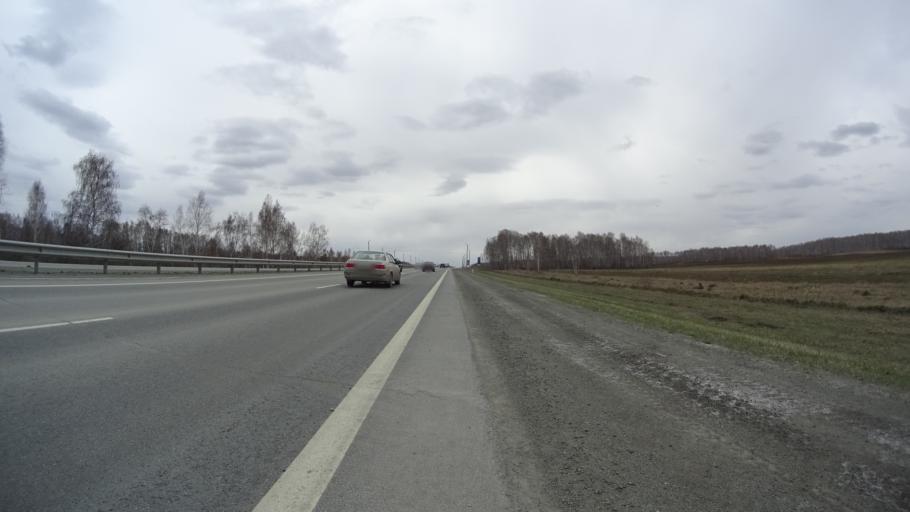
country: RU
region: Chelyabinsk
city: Yemanzhelinka
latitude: 54.8373
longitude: 61.3129
